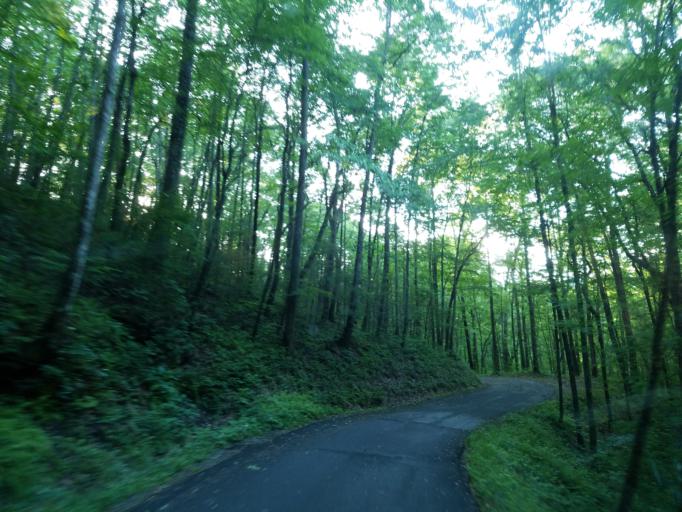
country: US
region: Georgia
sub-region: Union County
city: Blairsville
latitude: 34.7085
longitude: -84.0165
